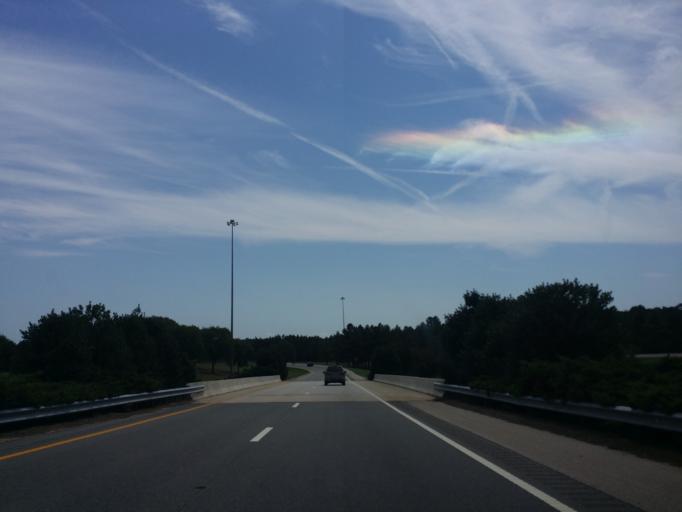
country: US
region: North Carolina
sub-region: Wake County
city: Morrisville
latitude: 35.8653
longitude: -78.8049
